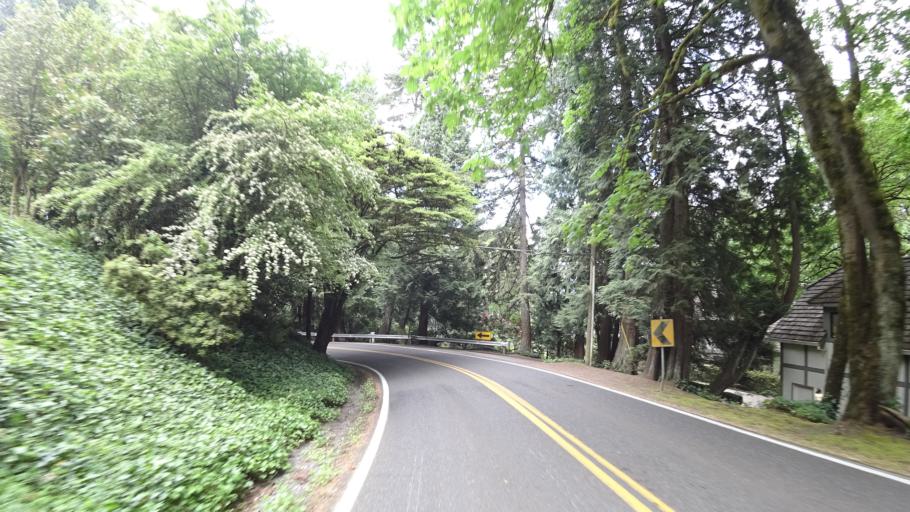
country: US
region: Oregon
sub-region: Clackamas County
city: Milwaukie
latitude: 45.4443
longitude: -122.6600
